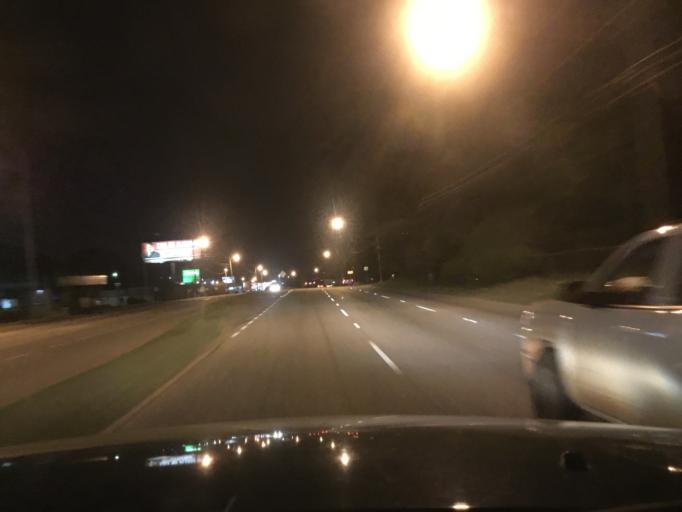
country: US
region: Alabama
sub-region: Montgomery County
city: Montgomery
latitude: 32.3848
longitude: -86.2527
